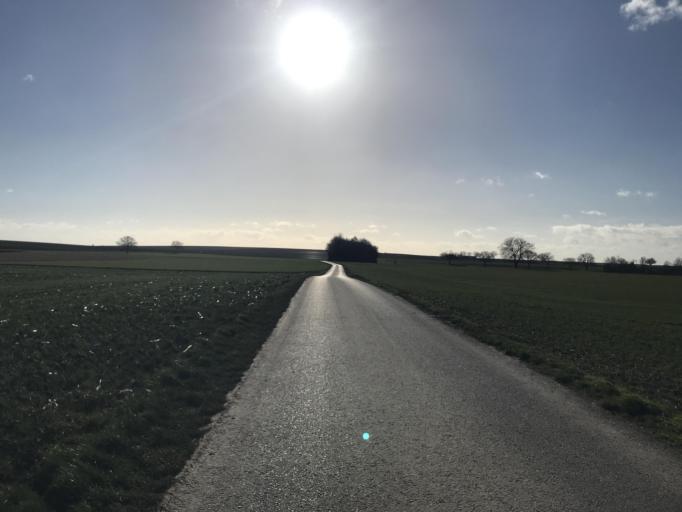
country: DE
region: Rheinland-Pfalz
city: Lorzweiler
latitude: 49.8906
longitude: 8.3142
